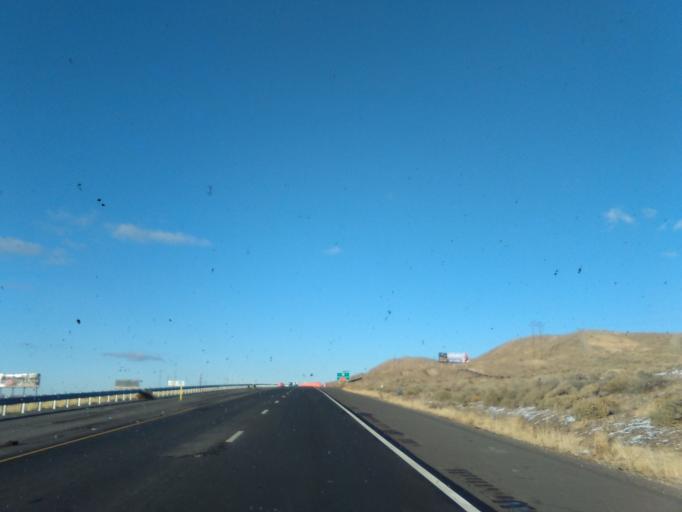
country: US
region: New Mexico
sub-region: Bernalillo County
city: South Valley
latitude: 35.0108
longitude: -106.6414
